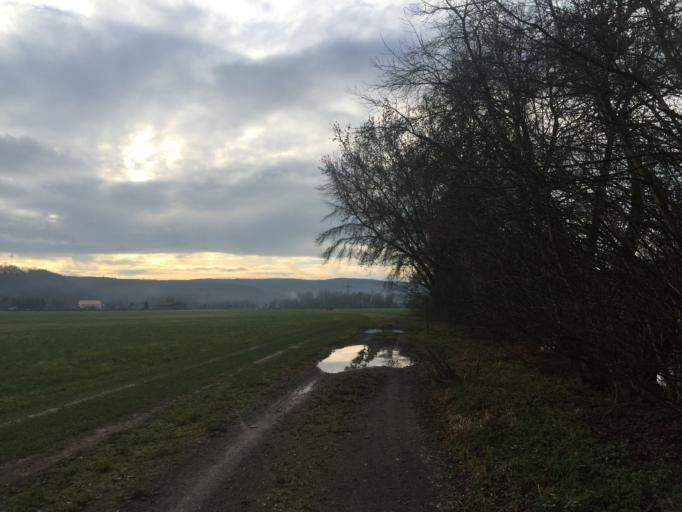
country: DE
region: Thuringia
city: Orlamunde
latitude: 50.7646
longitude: 11.5202
